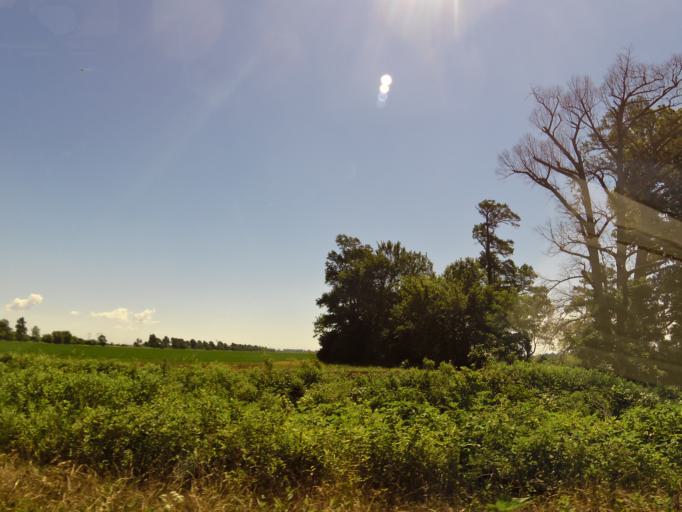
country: US
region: Missouri
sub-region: New Madrid County
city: Lilbourn
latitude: 36.5731
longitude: -89.7027
